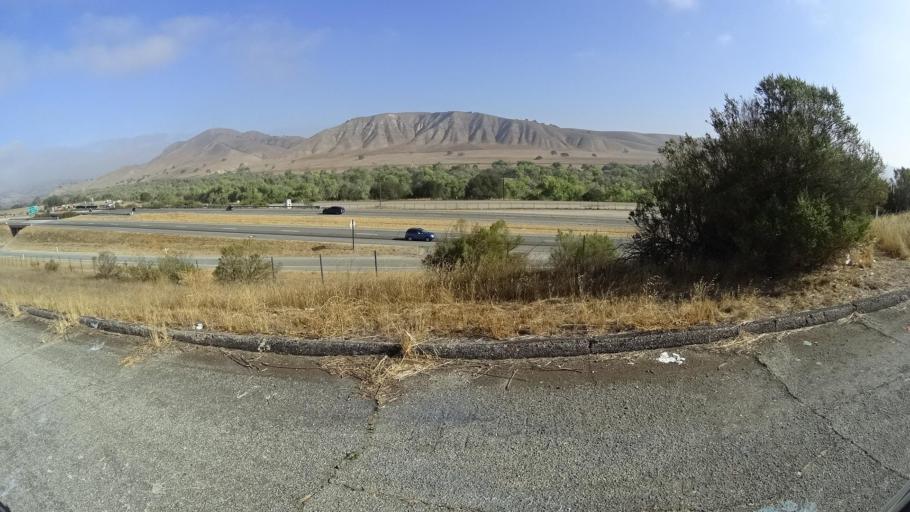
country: US
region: California
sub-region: San Luis Obispo County
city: Lake Nacimiento
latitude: 35.8631
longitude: -120.8178
